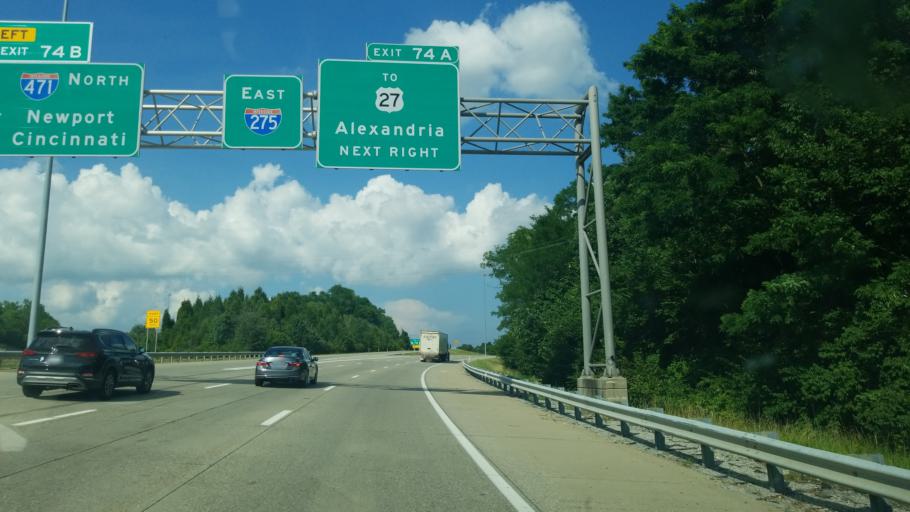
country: US
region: Kentucky
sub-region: Campbell County
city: Highland Heights
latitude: 39.0437
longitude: -84.4676
